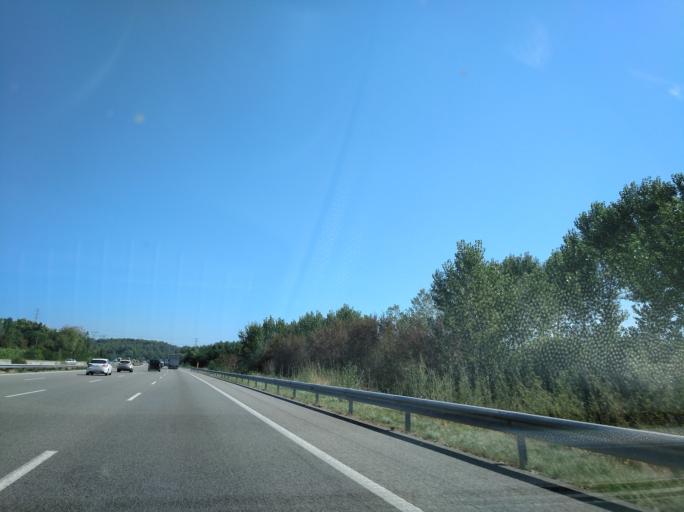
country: ES
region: Catalonia
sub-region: Provincia de Girona
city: Celra
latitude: 42.0490
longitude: 2.8733
